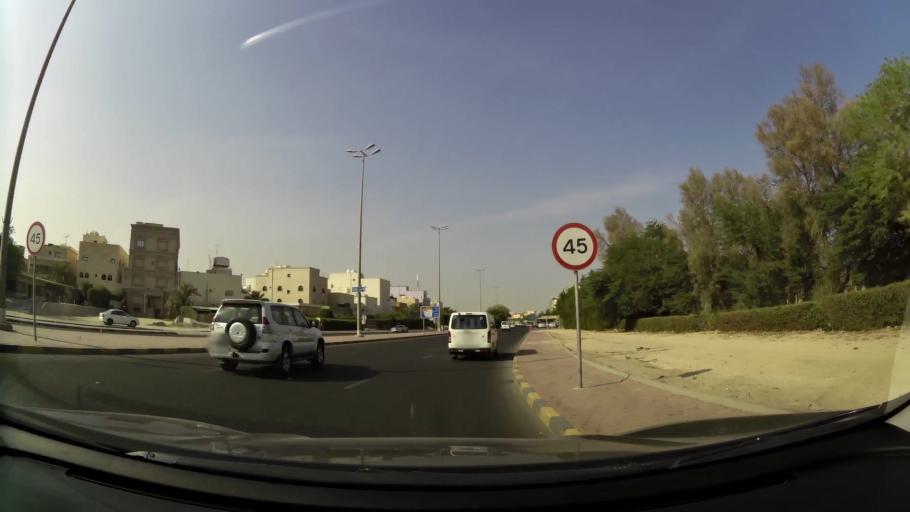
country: KW
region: Mubarak al Kabir
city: Mubarak al Kabir
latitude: 29.1756
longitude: 48.0844
